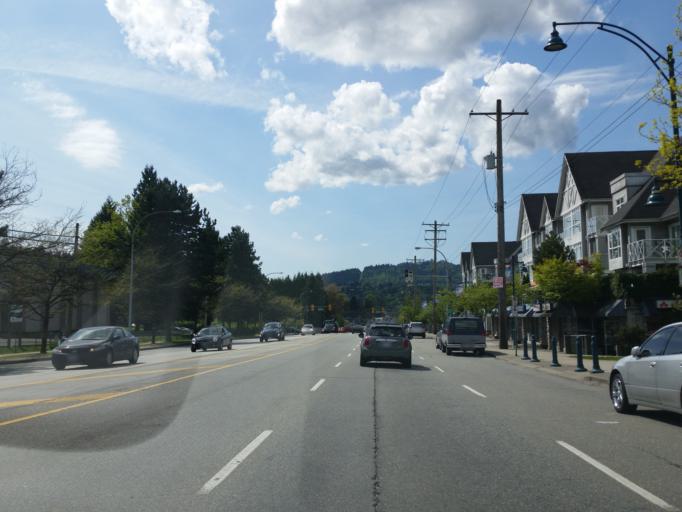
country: CA
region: British Columbia
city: Port Moody
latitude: 49.2767
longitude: -122.8377
